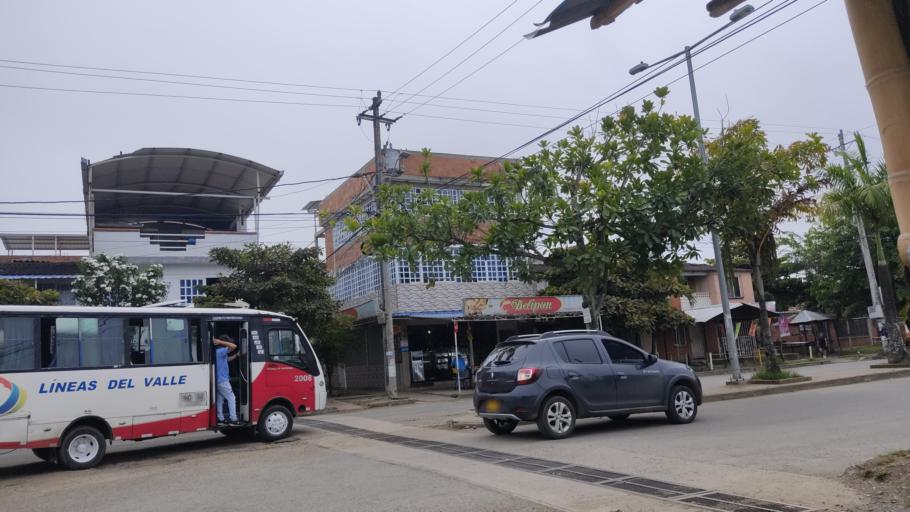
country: CO
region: Valle del Cauca
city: Jamundi
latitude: 3.2388
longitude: -76.5096
